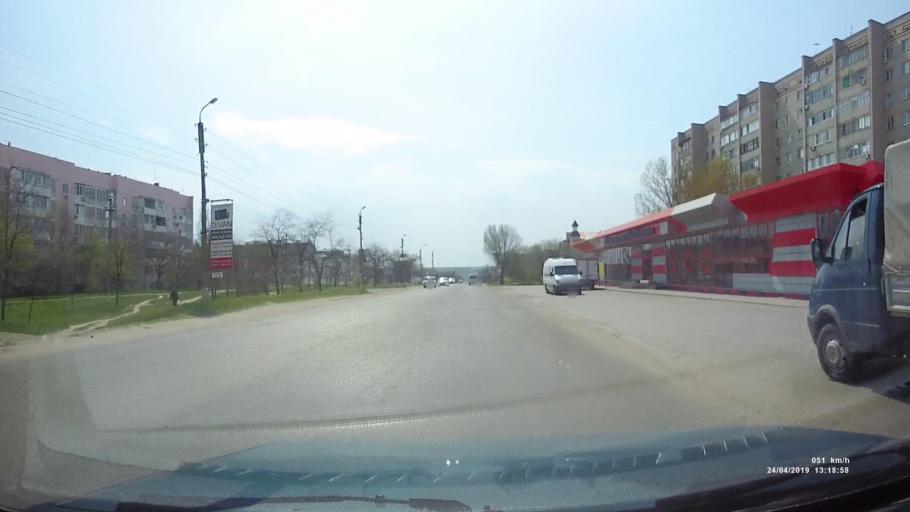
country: RU
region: Kalmykiya
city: Elista
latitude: 46.3022
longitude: 44.2935
